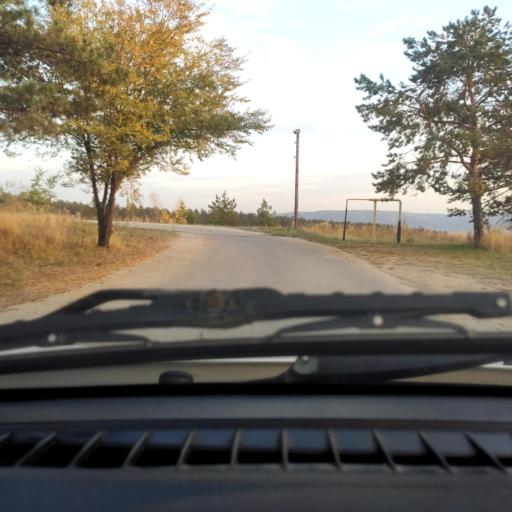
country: RU
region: Samara
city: Zhigulevsk
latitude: 53.4841
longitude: 49.5390
